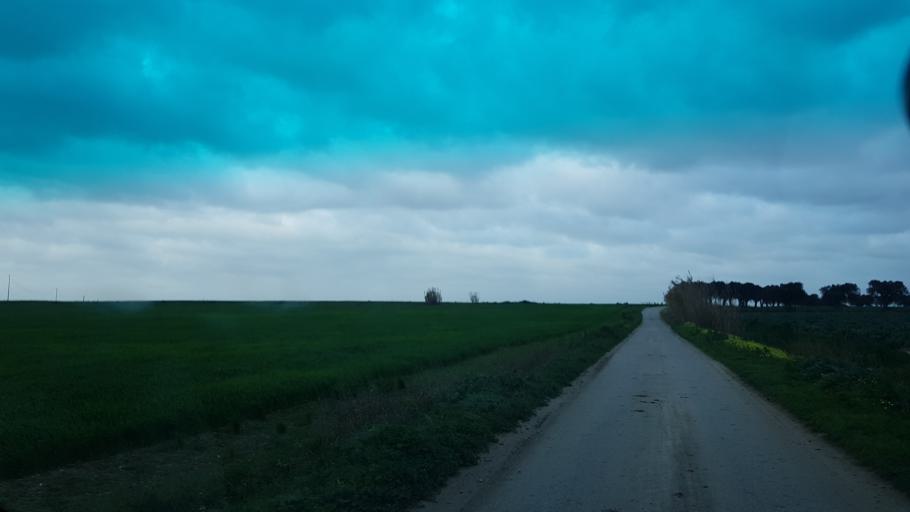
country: IT
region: Apulia
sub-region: Provincia di Brindisi
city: La Rosa
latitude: 40.5965
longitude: 17.9702
